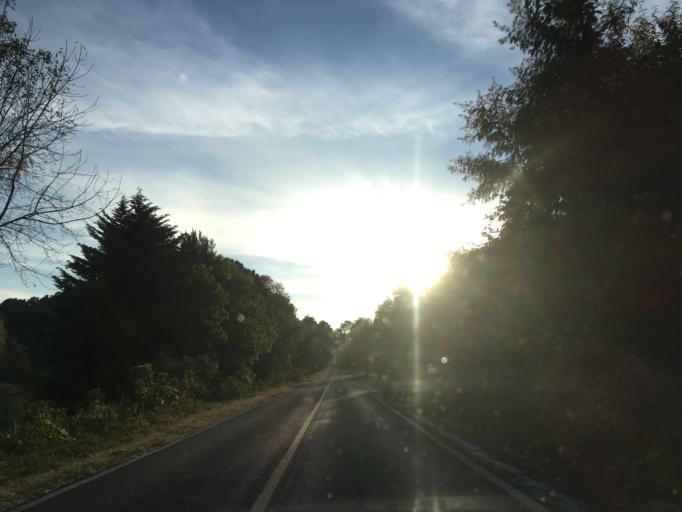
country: MX
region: Michoacan
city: Tzitzio
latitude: 19.6521
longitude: -100.9378
